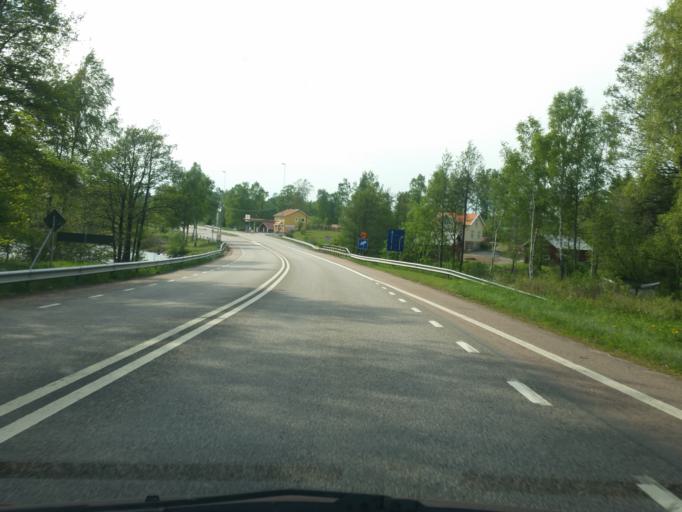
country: SE
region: Vaestra Goetaland
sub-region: Ulricehamns Kommun
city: Ulricehamn
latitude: 57.8128
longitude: 13.2925
